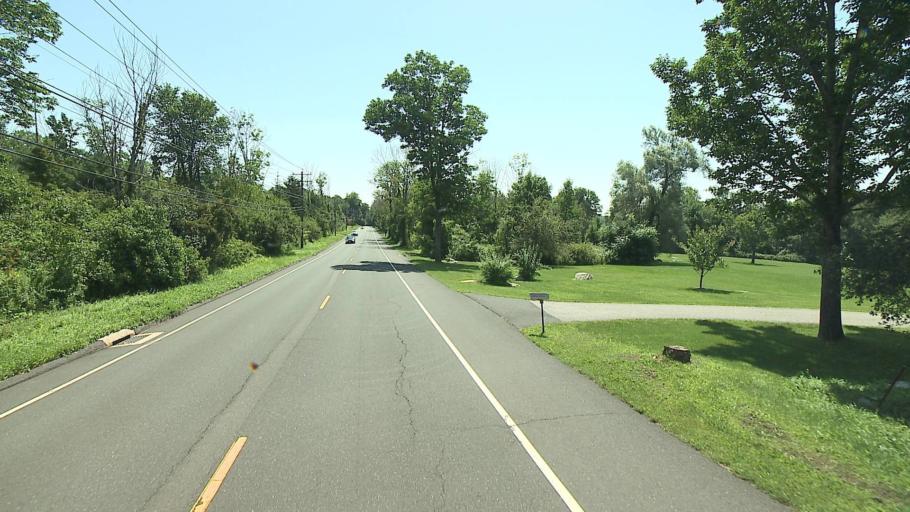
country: US
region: Connecticut
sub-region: Litchfield County
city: Litchfield
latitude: 41.8416
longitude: -73.2786
